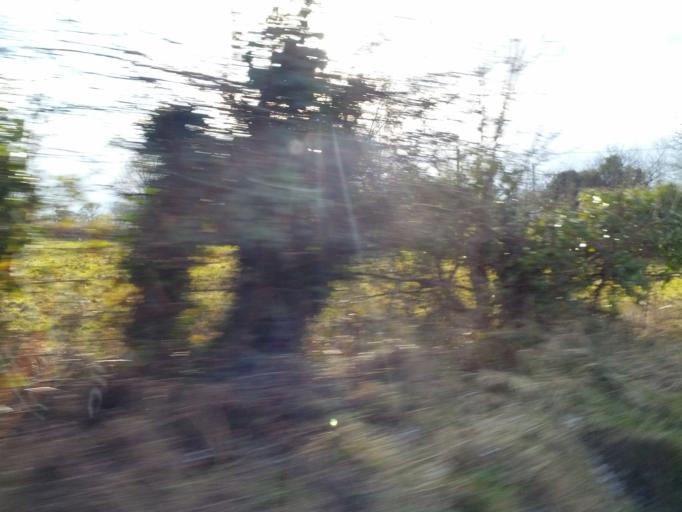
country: IE
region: Connaught
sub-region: County Galway
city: Athenry
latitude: 53.3866
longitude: -8.6000
